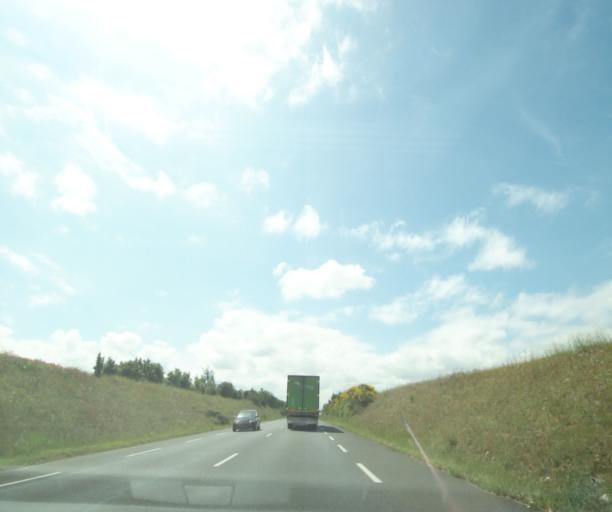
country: FR
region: Poitou-Charentes
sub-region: Departement des Deux-Sevres
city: Louzy
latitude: 47.0042
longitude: -0.1944
